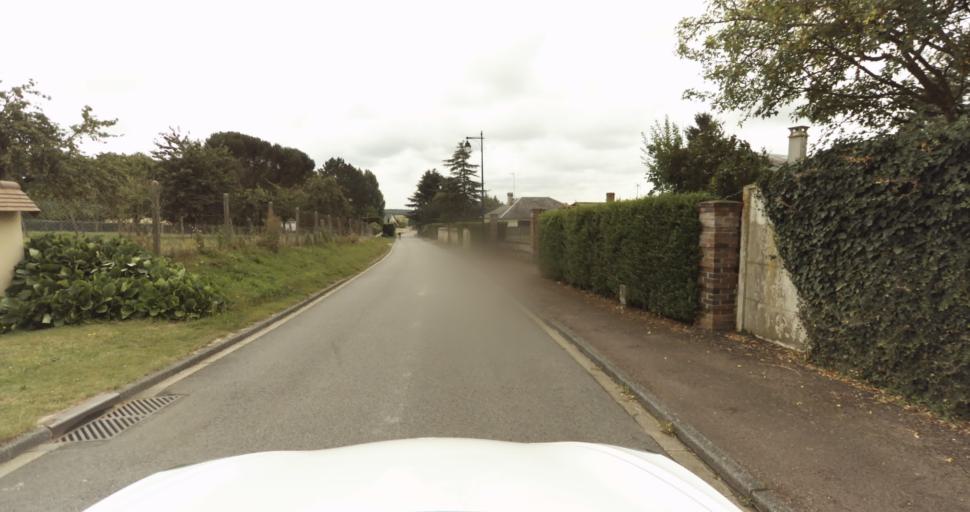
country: FR
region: Haute-Normandie
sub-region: Departement de l'Eure
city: Claville
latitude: 49.0228
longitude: 1.0334
